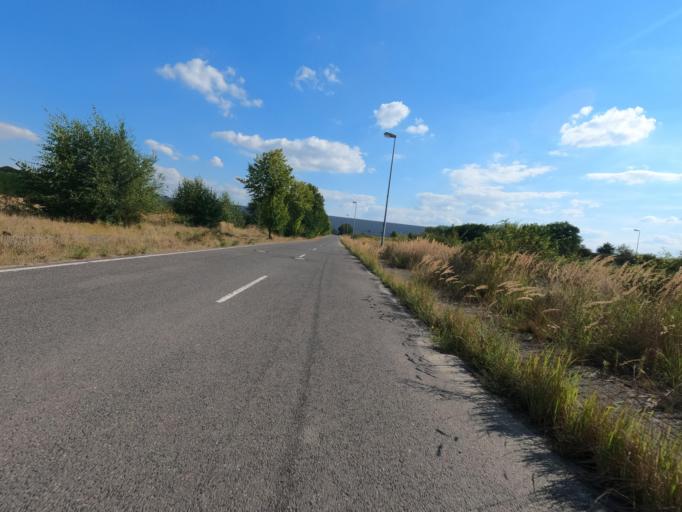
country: DE
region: North Rhine-Westphalia
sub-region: Regierungsbezirk Koln
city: Wassenberg
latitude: 51.0845
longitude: 6.1713
